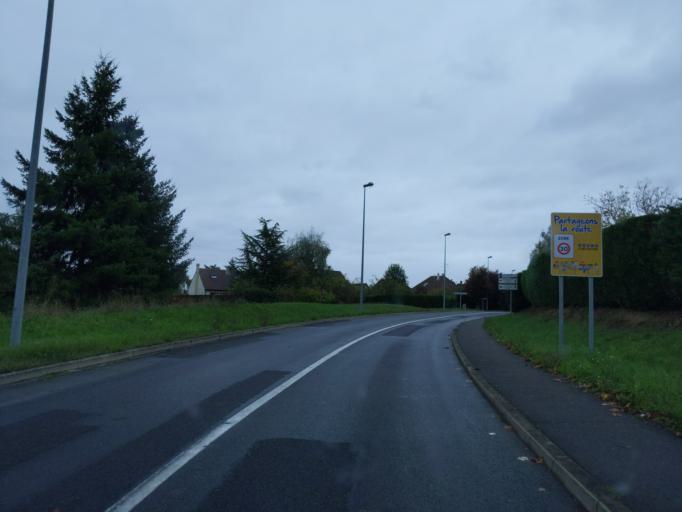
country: FR
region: Ile-de-France
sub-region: Departement des Yvelines
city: Saint-Arnoult-en-Yvelines
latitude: 48.5803
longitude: 1.9425
